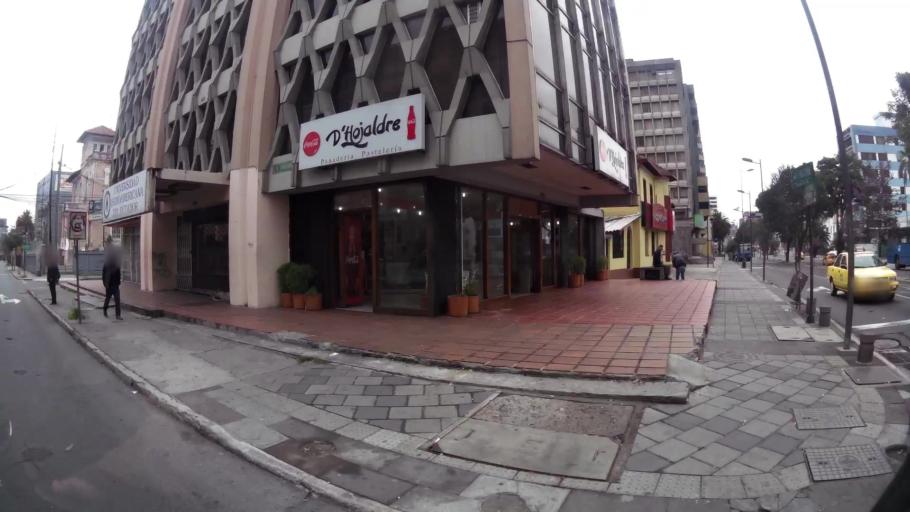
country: EC
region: Pichincha
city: Quito
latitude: -0.1989
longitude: -78.4939
